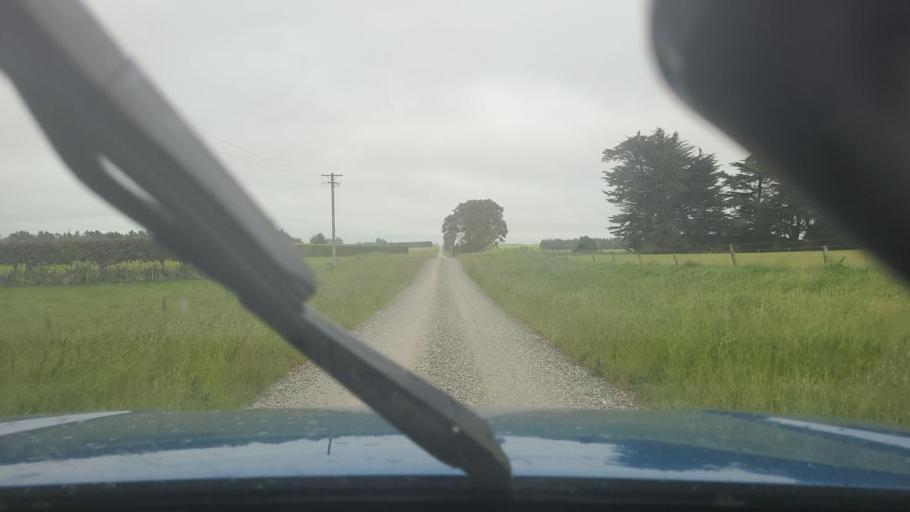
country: NZ
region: Southland
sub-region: Invercargill City
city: Invercargill
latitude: -46.2849
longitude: 168.5499
